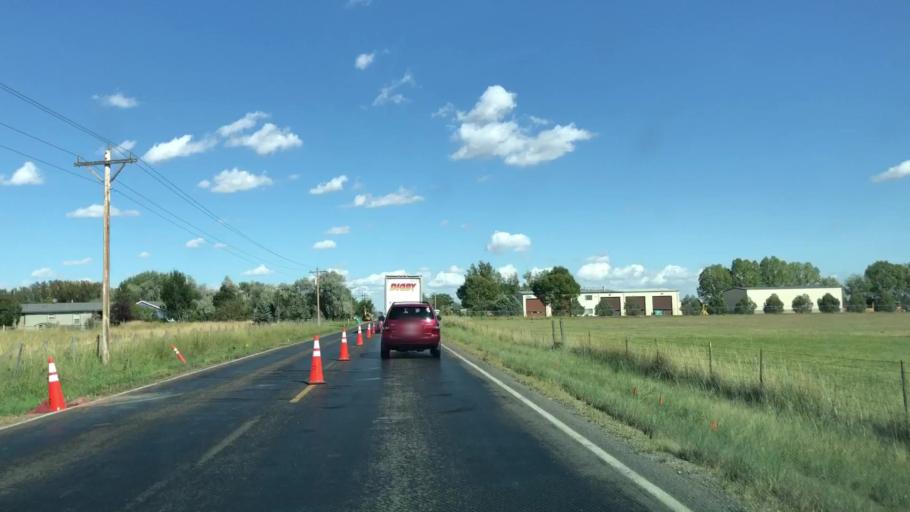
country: US
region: Colorado
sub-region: Larimer County
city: Wellington
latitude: 40.7547
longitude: -105.0797
